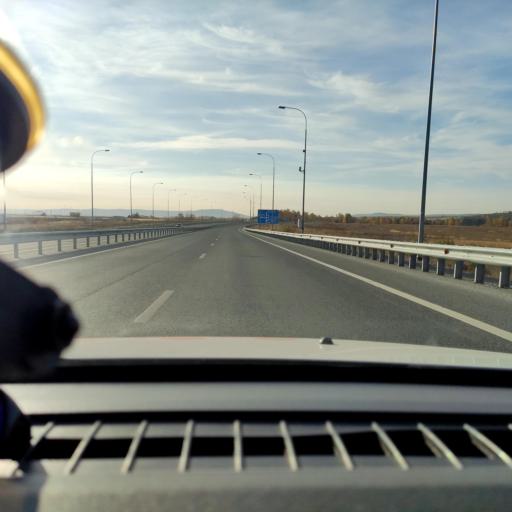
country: RU
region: Samara
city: Bereza
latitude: 53.4974
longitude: 50.1167
